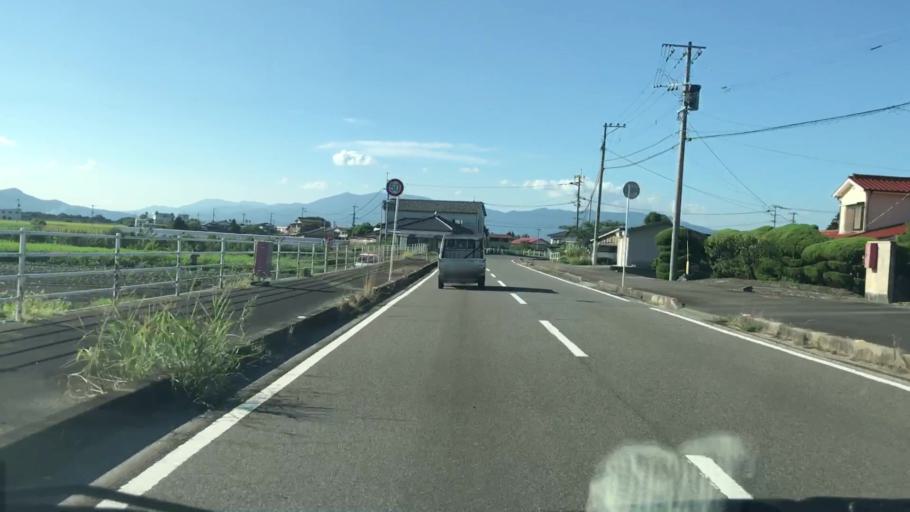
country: JP
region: Saga Prefecture
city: Saga-shi
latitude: 33.2005
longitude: 130.2662
